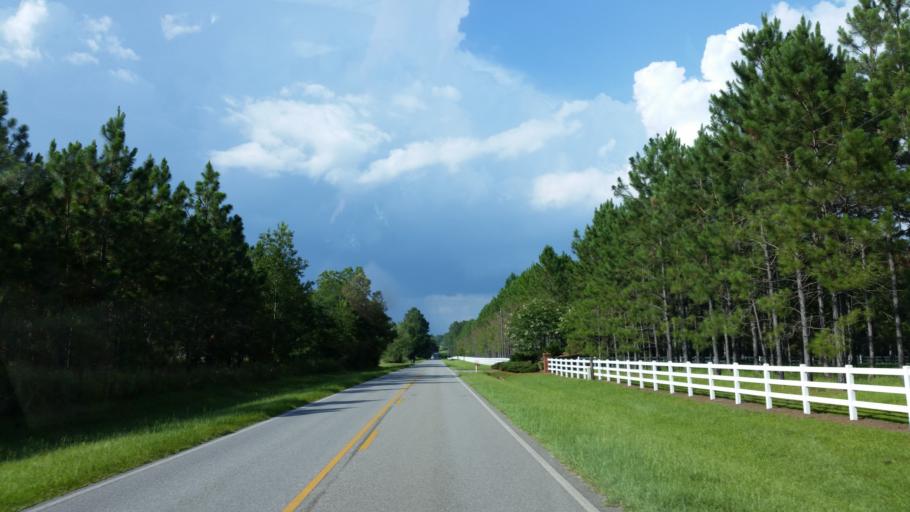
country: US
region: Georgia
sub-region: Lowndes County
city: Hahira
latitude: 30.9589
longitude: -83.4065
